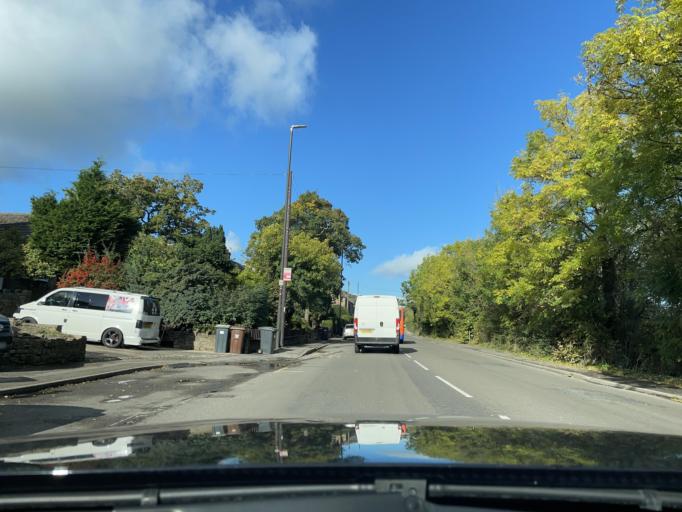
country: GB
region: England
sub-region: Derbyshire
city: New Mills
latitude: 53.3512
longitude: -1.9943
